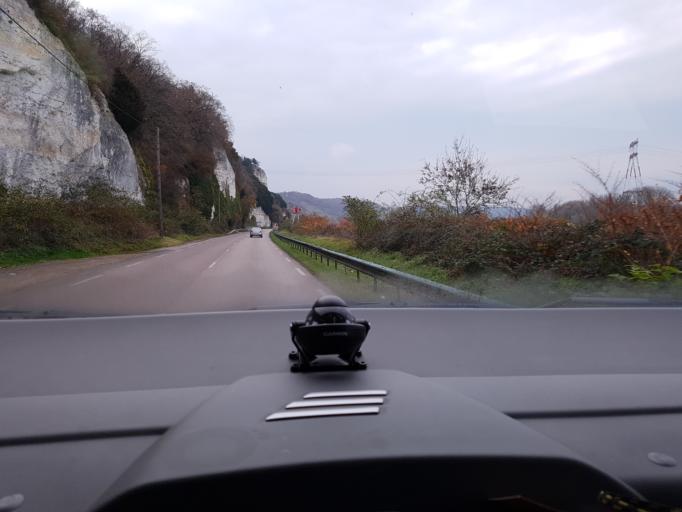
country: FR
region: Haute-Normandie
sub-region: Departement de la Seine-Maritime
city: Saint-Pierre-de-Varengeville
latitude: 49.4864
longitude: 0.9090
